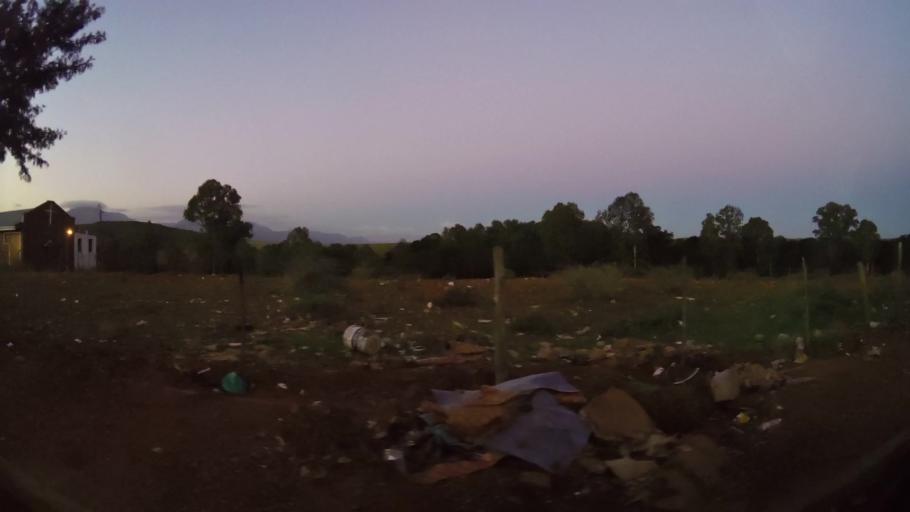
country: ZA
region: Western Cape
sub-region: Eden District Municipality
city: Riversdale
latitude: -34.1033
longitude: 21.2738
